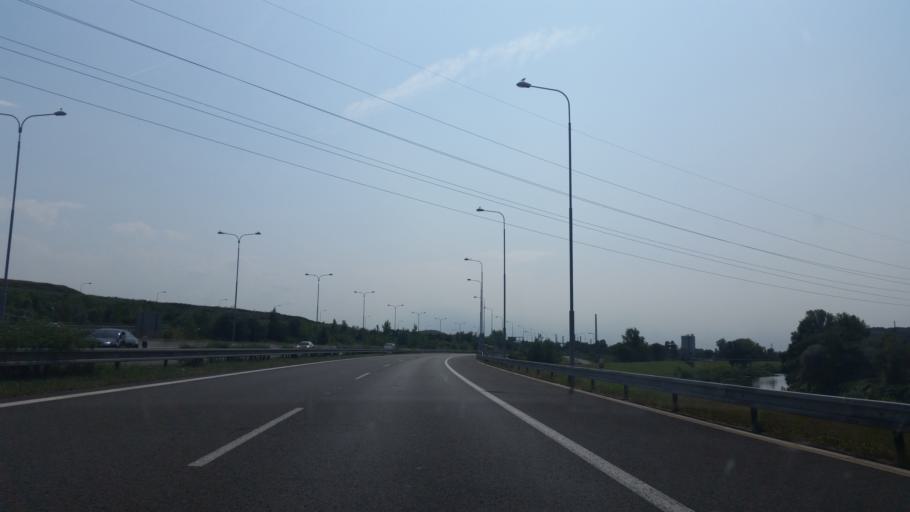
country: CZ
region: Moravskoslezsky
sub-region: Okres Ostrava-Mesto
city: Ostrava
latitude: 49.8780
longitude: 18.3035
